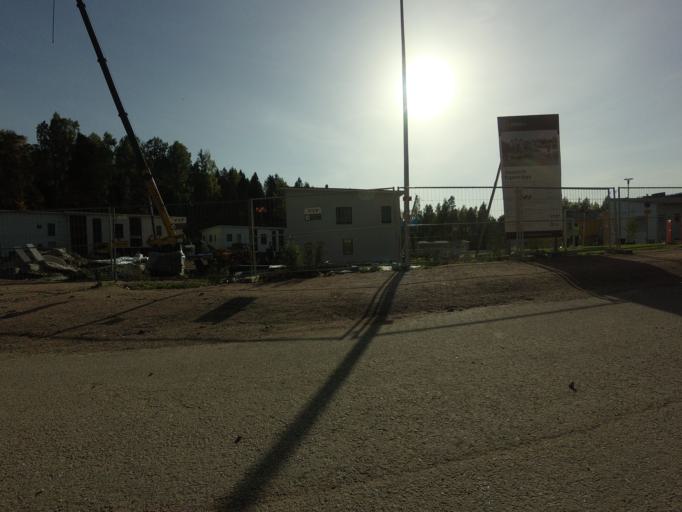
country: FI
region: Uusimaa
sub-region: Helsinki
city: Espoo
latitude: 60.1745
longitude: 24.6203
